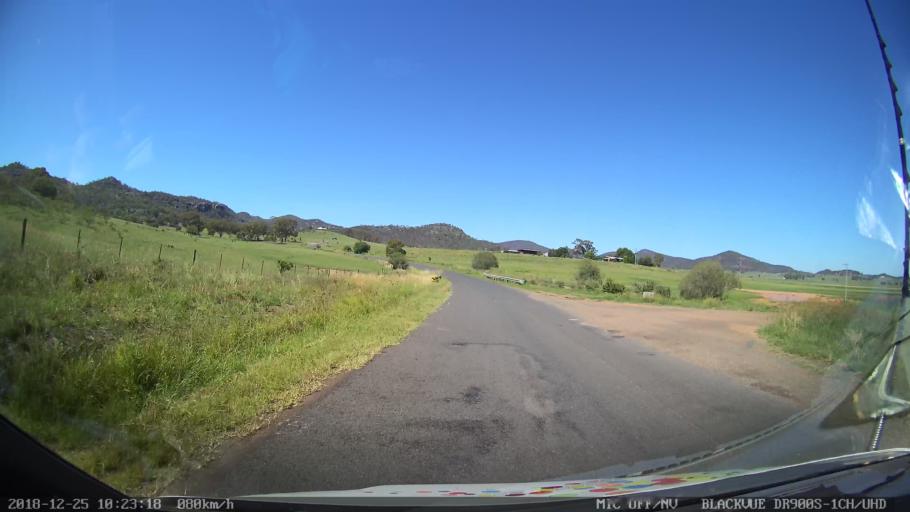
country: AU
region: New South Wales
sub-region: Muswellbrook
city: Denman
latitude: -32.3842
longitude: 150.5238
